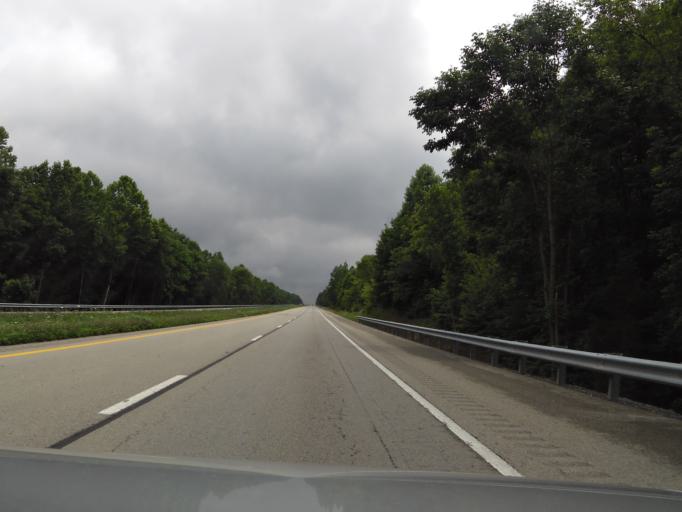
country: US
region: Kentucky
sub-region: Ohio County
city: Oak Grove
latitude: 37.3937
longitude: -86.5913
